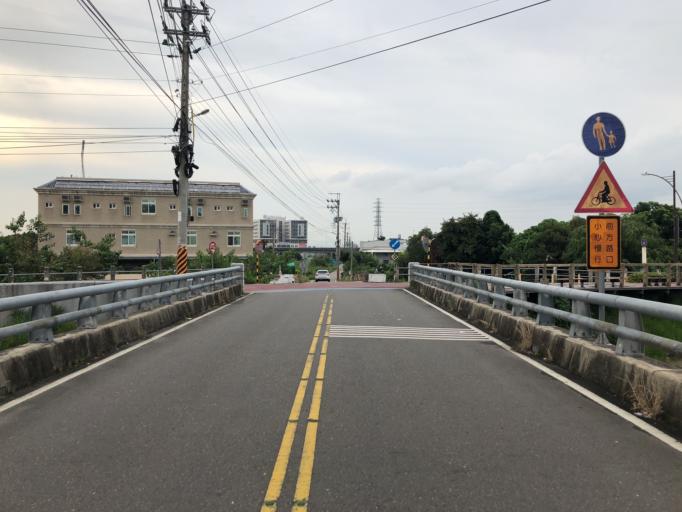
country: TW
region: Taiwan
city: Zhongxing New Village
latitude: 24.0485
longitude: 120.6904
